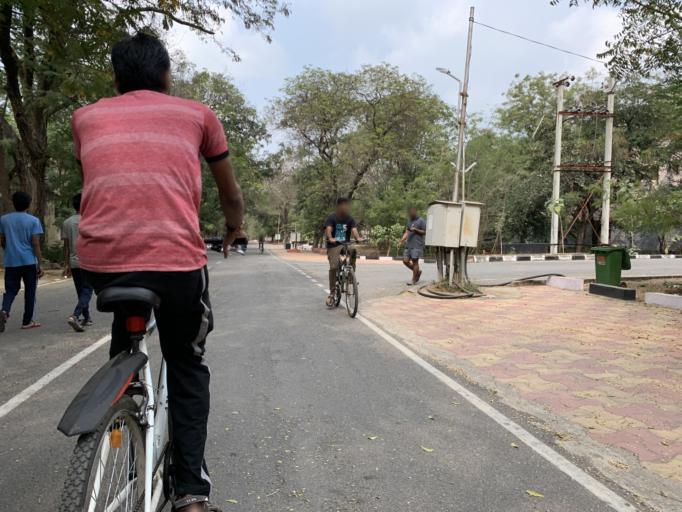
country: IN
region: Telangana
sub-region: Warangal
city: Warangal
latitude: 17.9822
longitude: 79.5321
